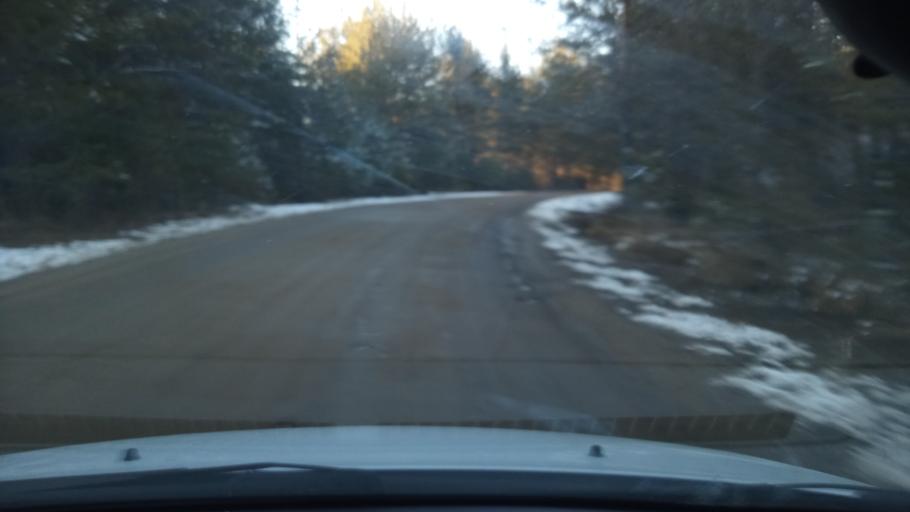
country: BG
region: Sofia-Capital
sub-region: Stolichna Obshtina
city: Sofia
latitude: 42.4887
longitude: 23.3823
